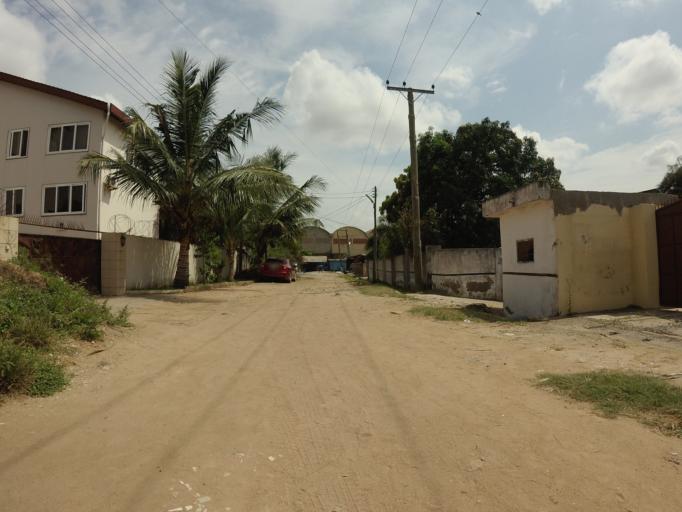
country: GH
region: Greater Accra
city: Dome
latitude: 5.6358
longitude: -0.2379
